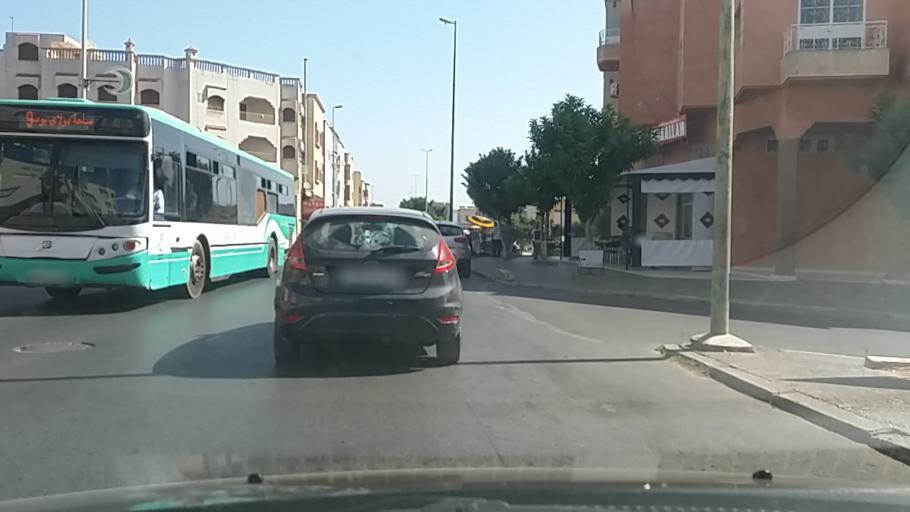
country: MA
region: Gharb-Chrarda-Beni Hssen
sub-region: Kenitra Province
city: Kenitra
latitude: 34.2712
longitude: -6.6099
